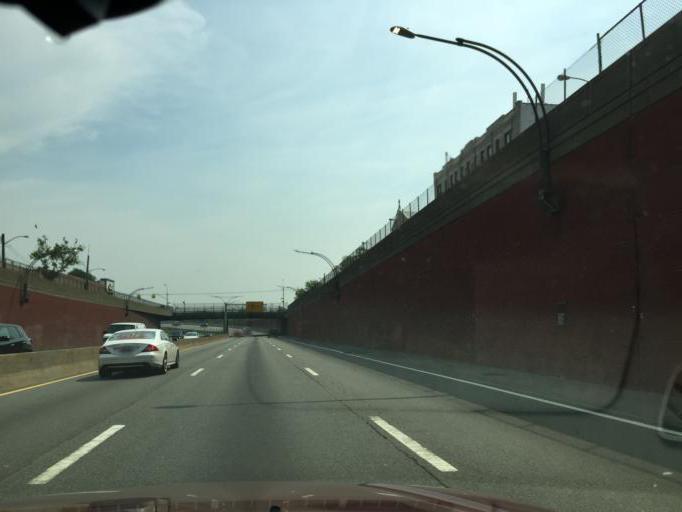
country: US
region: New York
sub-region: Bronx
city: The Bronx
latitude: 40.8334
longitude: -73.8277
